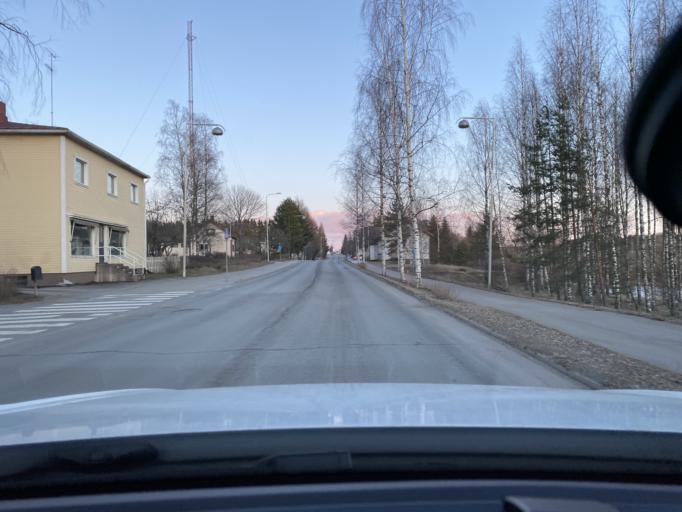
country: FI
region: Pirkanmaa
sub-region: Lounais-Pirkanmaa
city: Punkalaidun
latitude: 61.1163
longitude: 23.0896
